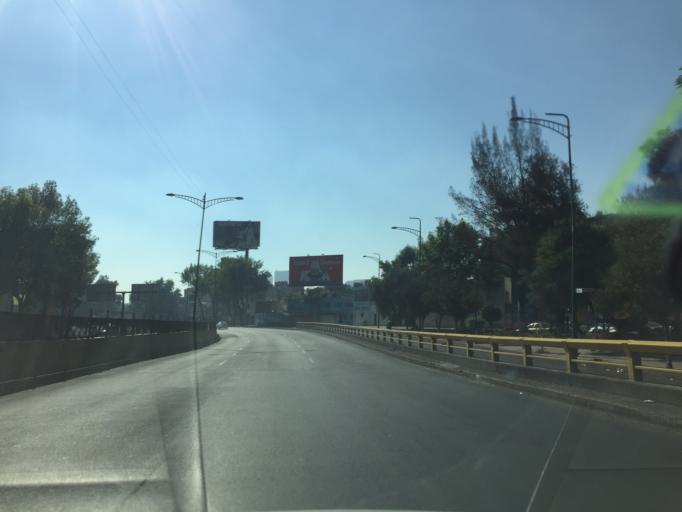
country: MX
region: Mexico City
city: Miguel Hidalgo
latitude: 19.4565
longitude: -99.1888
